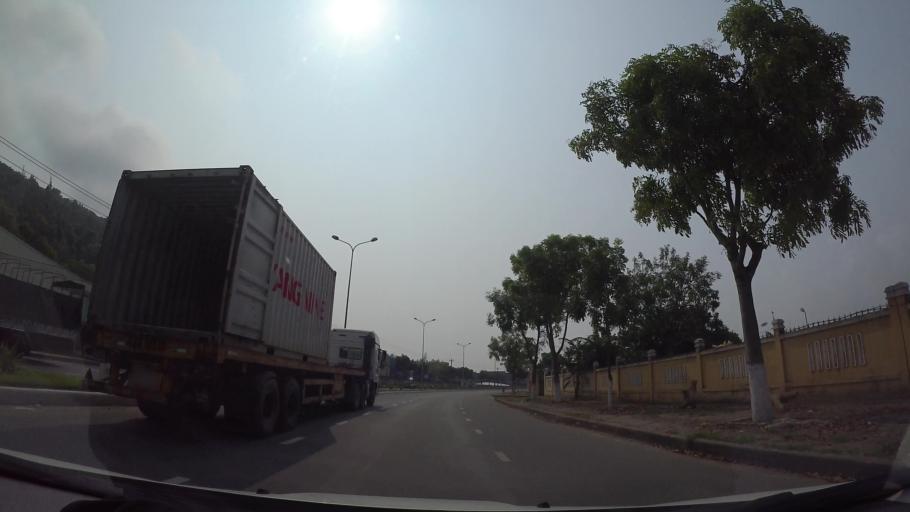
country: VN
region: Da Nang
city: Da Nang
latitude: 16.1130
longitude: 108.2438
